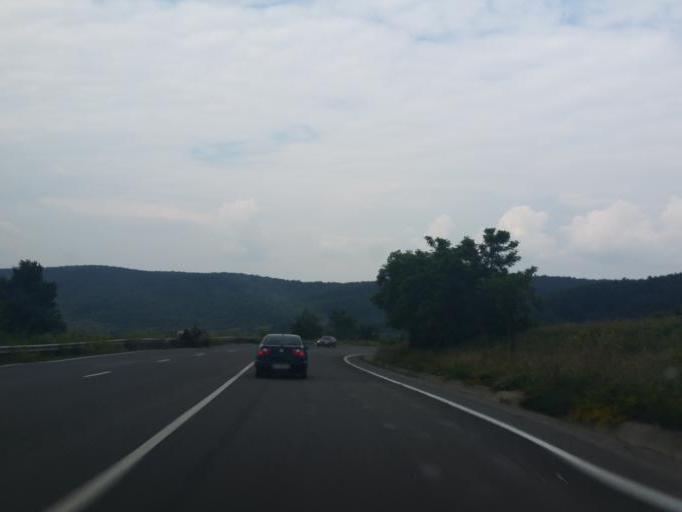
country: RO
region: Cluj
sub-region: Comuna Sanpaul
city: Sanpaul
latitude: 46.9441
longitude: 23.3824
